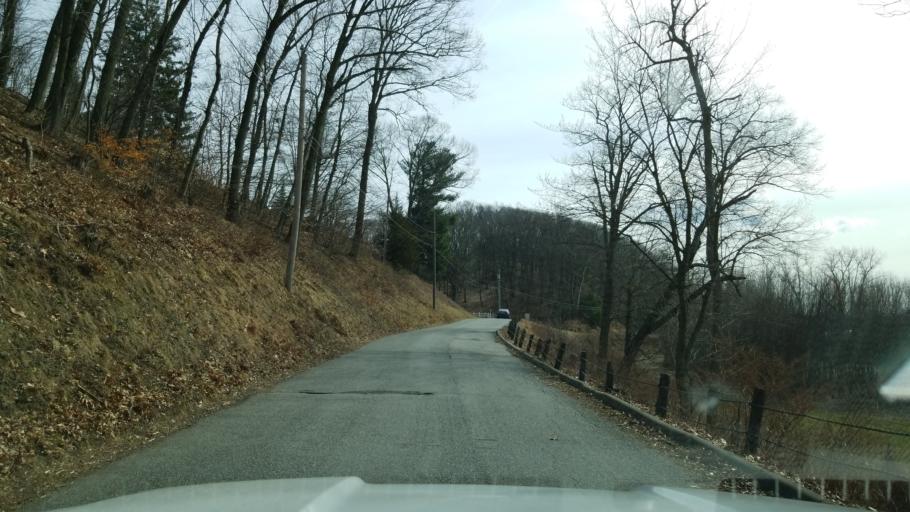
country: US
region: Connecticut
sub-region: Hartford County
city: Glastonbury Center
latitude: 41.6529
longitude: -72.6192
